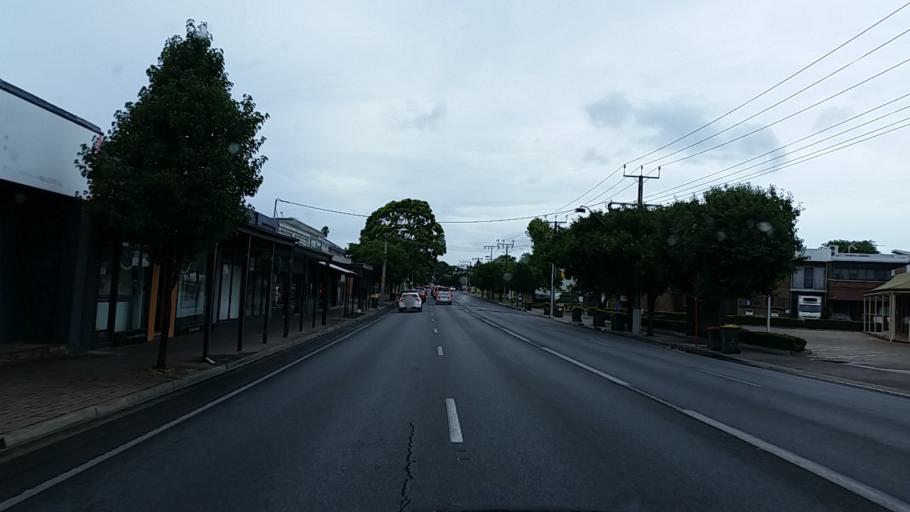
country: AU
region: South Australia
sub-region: Norwood Payneham St Peters
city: Trinity Gardens
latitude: -34.9144
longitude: 138.6237
